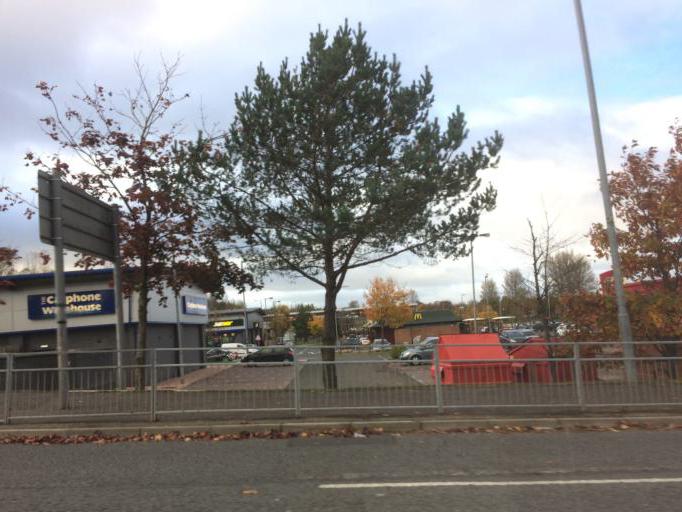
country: GB
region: Scotland
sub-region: East Renfrewshire
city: Newton Mearns
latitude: 55.8045
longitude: -4.3395
